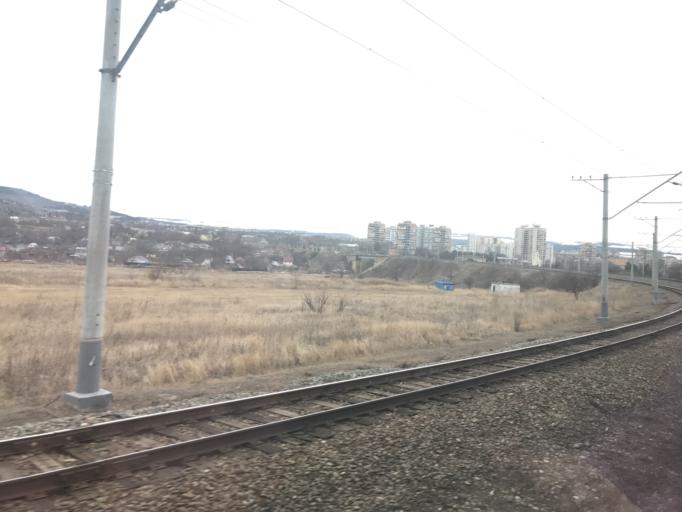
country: RU
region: Stavropol'skiy
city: Kislovodsk
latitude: 43.9466
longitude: 42.7328
